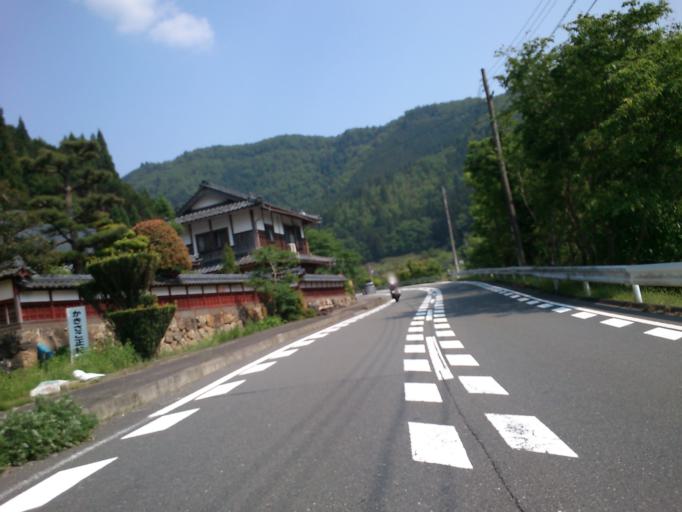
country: JP
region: Kyoto
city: Kameoka
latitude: 35.2331
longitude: 135.5706
